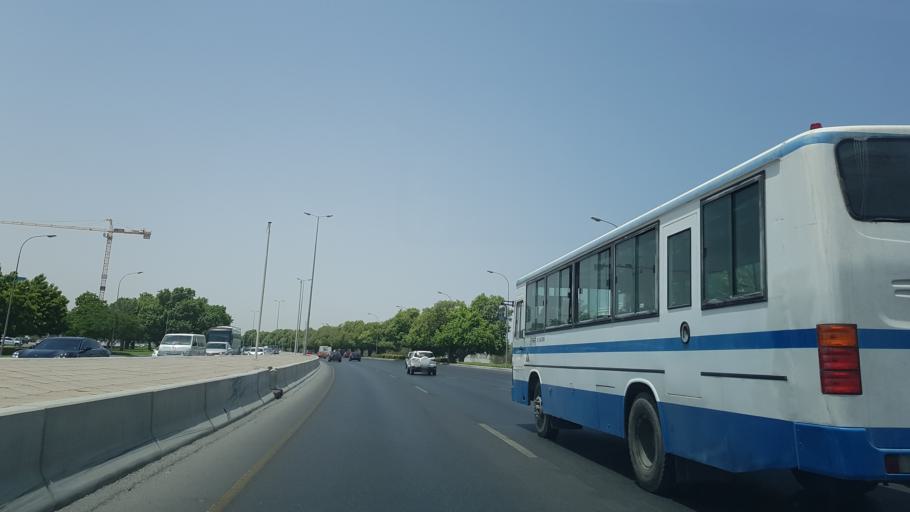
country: OM
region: Muhafazat Masqat
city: Bawshar
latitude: 23.5908
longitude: 58.3739
